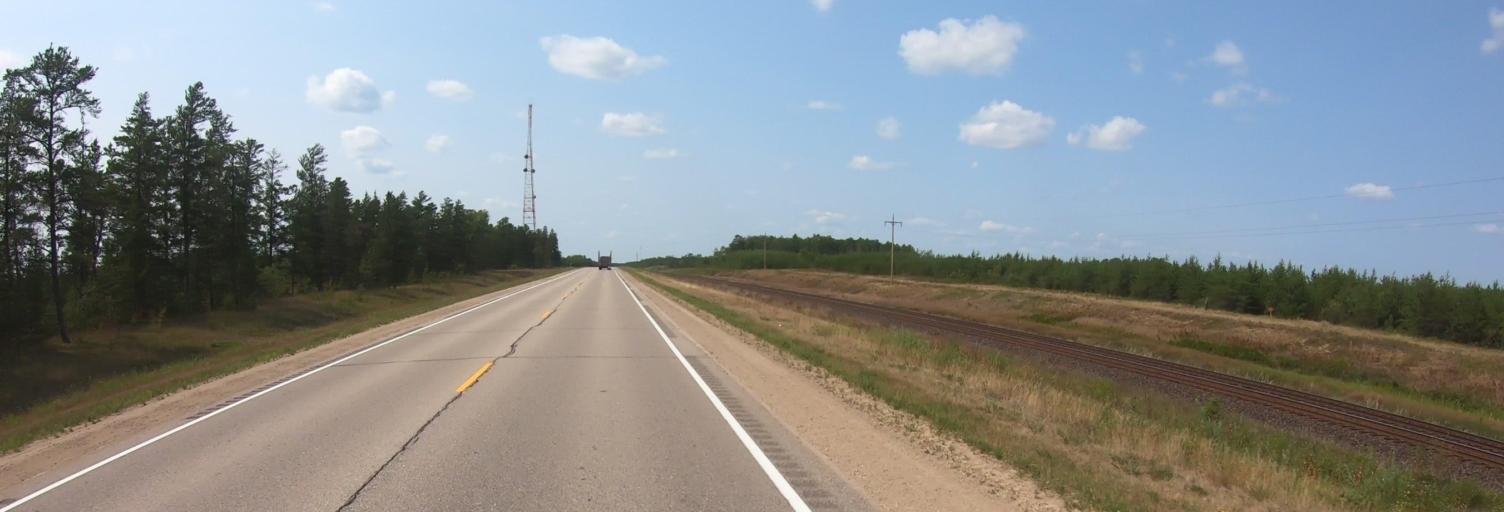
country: US
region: Minnesota
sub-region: Roseau County
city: Warroad
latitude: 48.7880
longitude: -95.0444
